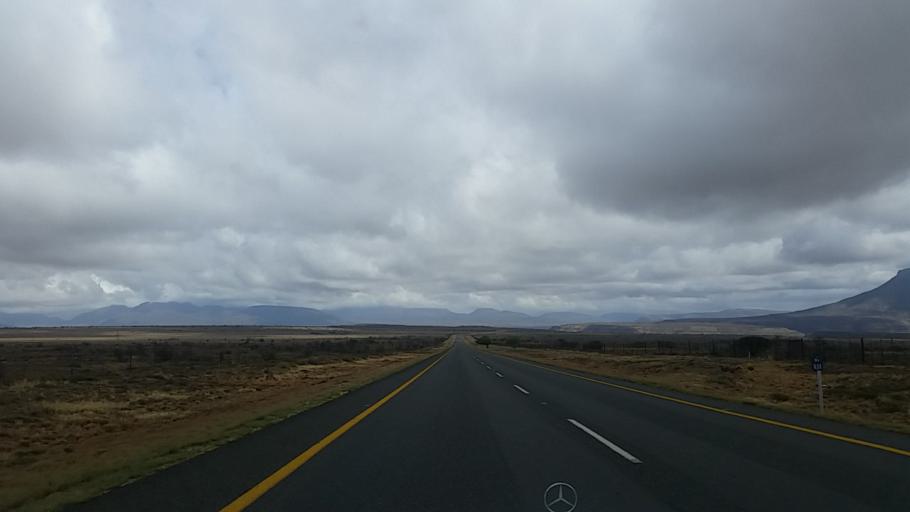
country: ZA
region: Eastern Cape
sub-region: Cacadu District Municipality
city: Graaff-Reinet
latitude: -32.1216
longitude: 24.6026
